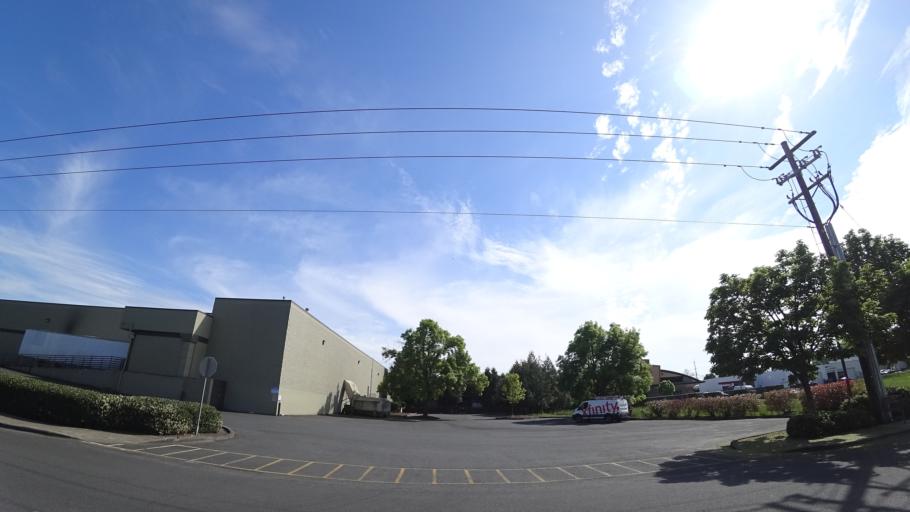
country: US
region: Oregon
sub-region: Washington County
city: Aloha
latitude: 45.4974
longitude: -122.8887
